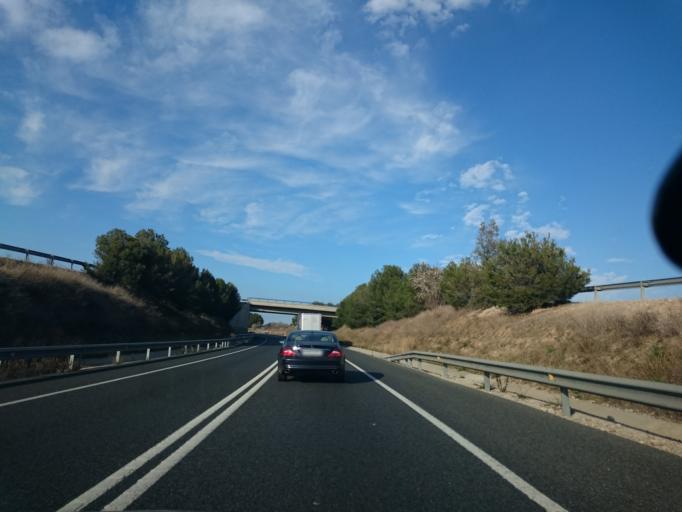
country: ES
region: Catalonia
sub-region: Provincia de Barcelona
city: Castellet
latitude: 41.3111
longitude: 1.6394
